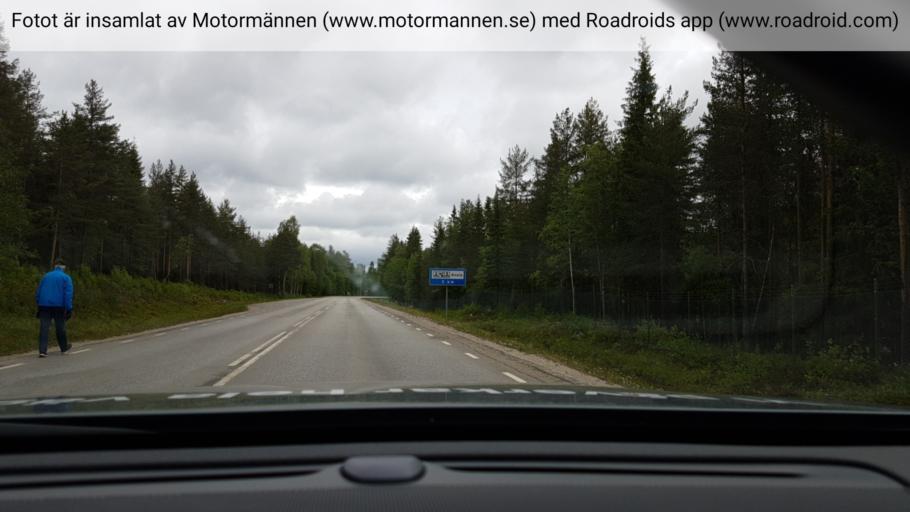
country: SE
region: Vaesterbotten
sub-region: Lycksele Kommun
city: Lycksele
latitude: 64.5808
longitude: 18.6581
